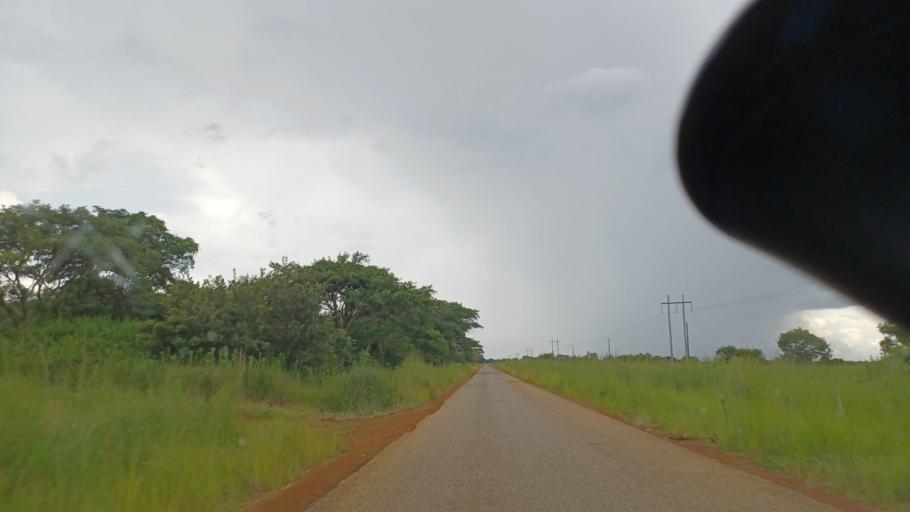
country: ZM
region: North-Western
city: Kasempa
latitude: -13.0310
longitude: 25.9969
